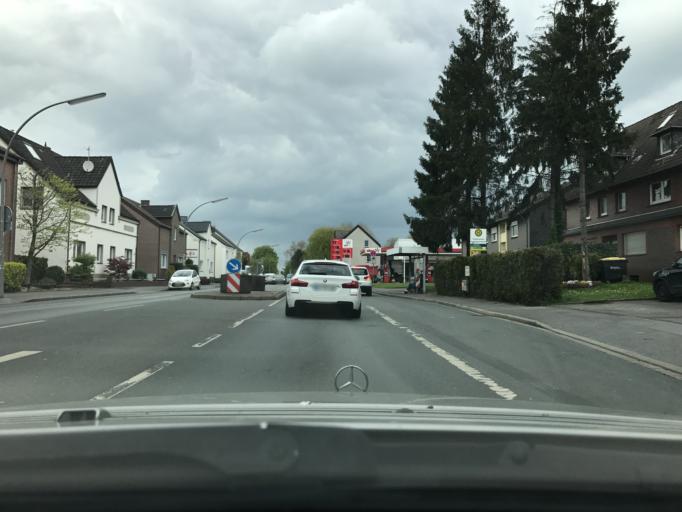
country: DE
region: North Rhine-Westphalia
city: Waltrop
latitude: 51.6119
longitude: 7.3940
